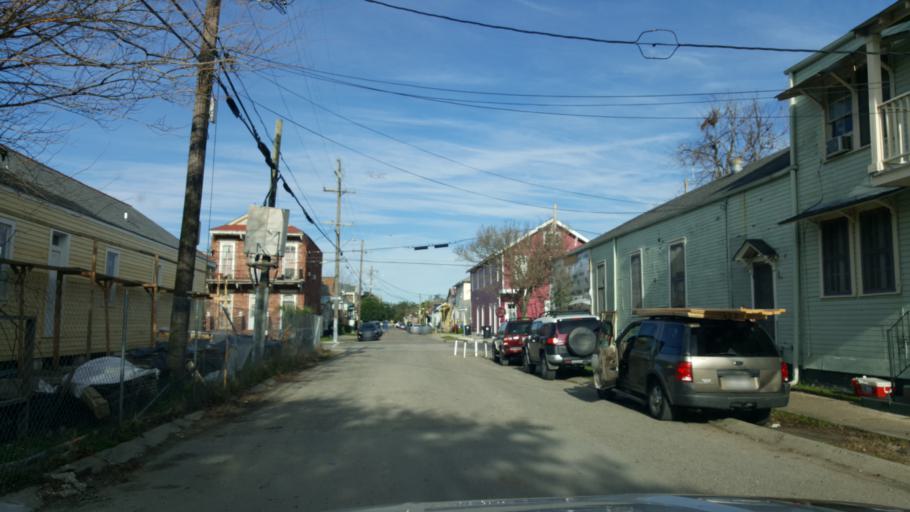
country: US
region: Louisiana
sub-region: Orleans Parish
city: New Orleans
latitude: 29.9707
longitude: -90.0739
